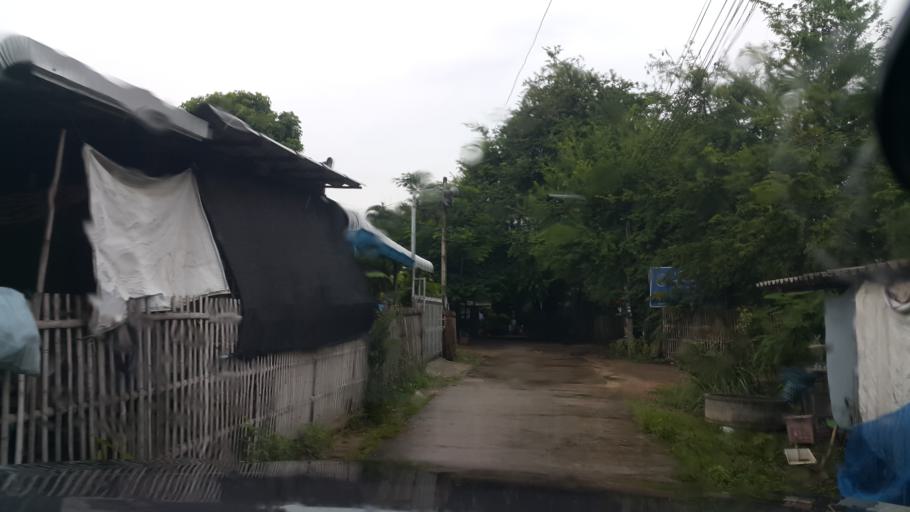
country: TH
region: Lamphun
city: Ban Thi
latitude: 18.6223
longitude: 99.1151
